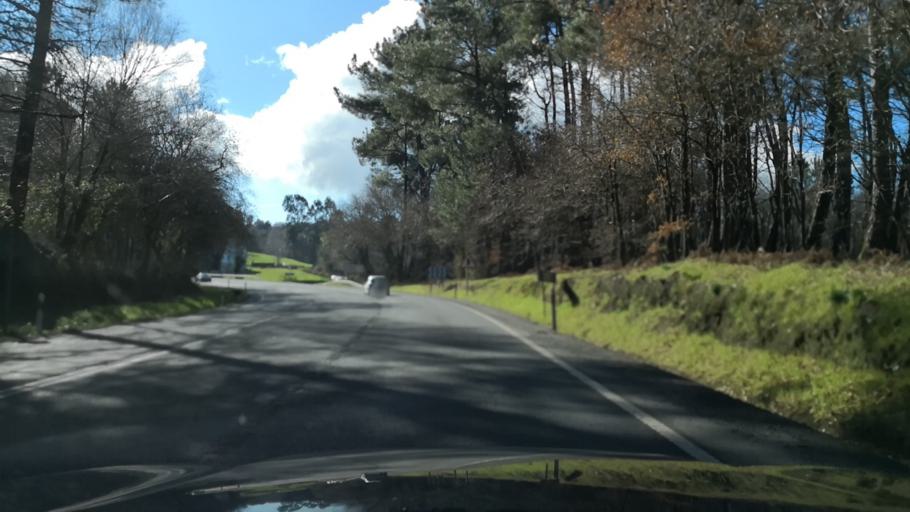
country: ES
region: Galicia
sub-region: Provincia de Pontevedra
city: Silleda
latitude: 42.7050
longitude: -8.3087
